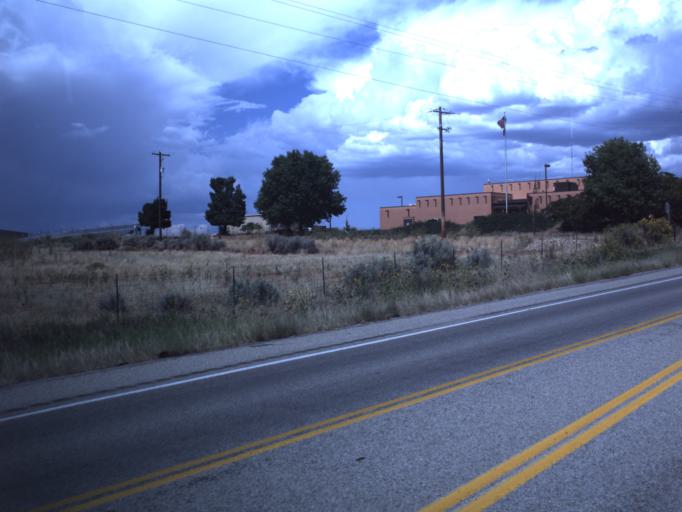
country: US
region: Utah
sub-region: San Juan County
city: Blanding
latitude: 37.5804
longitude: -109.4781
